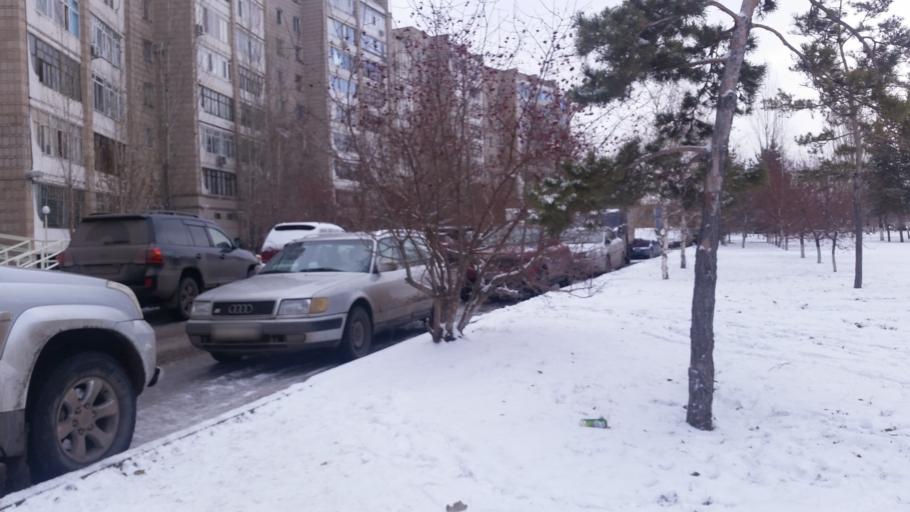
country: KZ
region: Astana Qalasy
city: Astana
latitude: 51.1618
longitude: 71.4680
